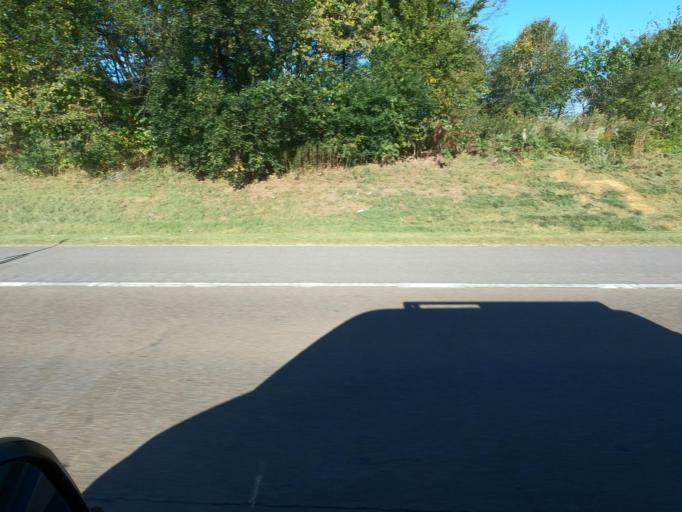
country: US
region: Tennessee
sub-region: Tipton County
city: Atoka
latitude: 35.4663
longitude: -89.7580
